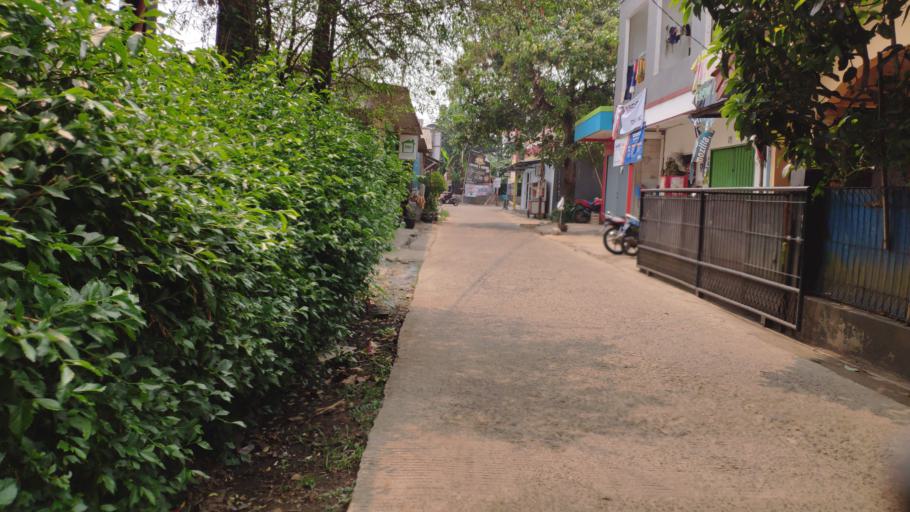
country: ID
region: West Java
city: Depok
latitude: -6.3709
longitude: 106.8006
